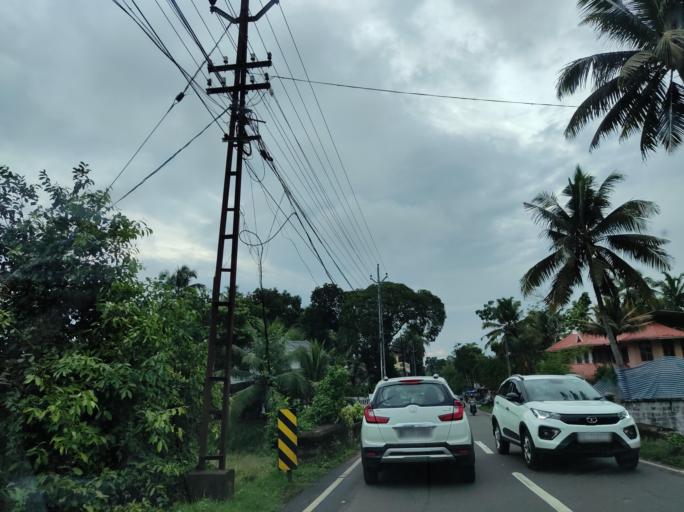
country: IN
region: Kerala
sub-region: Alappuzha
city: Mavelikara
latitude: 9.2518
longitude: 76.5179
